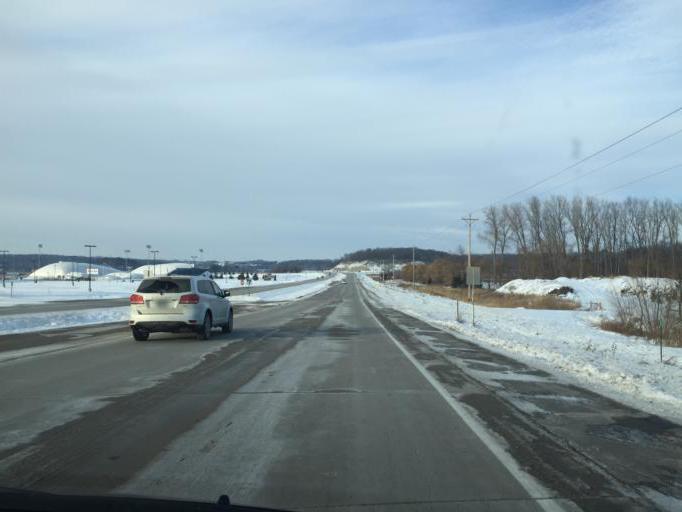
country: US
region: Minnesota
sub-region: Olmsted County
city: Rochester
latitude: 44.0141
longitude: -92.4192
